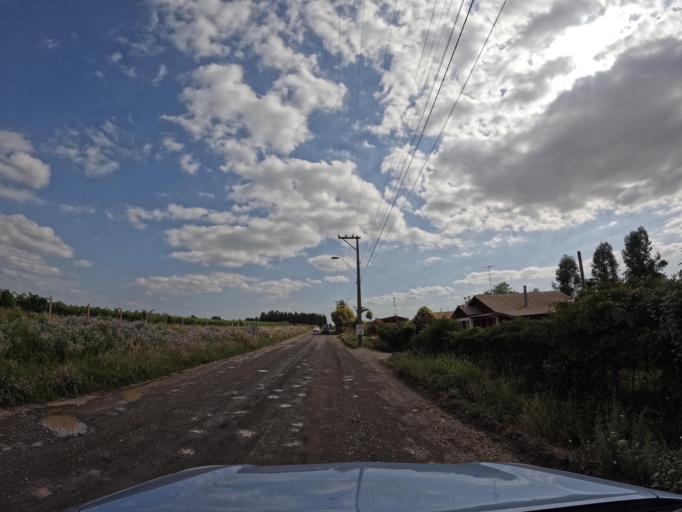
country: CL
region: Maule
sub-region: Provincia de Curico
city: Molina
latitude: -35.1636
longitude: -71.2884
